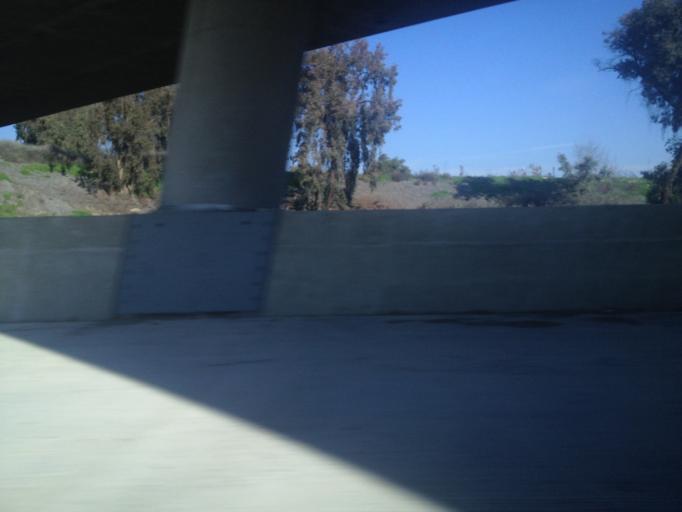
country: US
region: California
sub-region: Fresno County
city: Kingsburg
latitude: 36.5067
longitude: -119.5482
